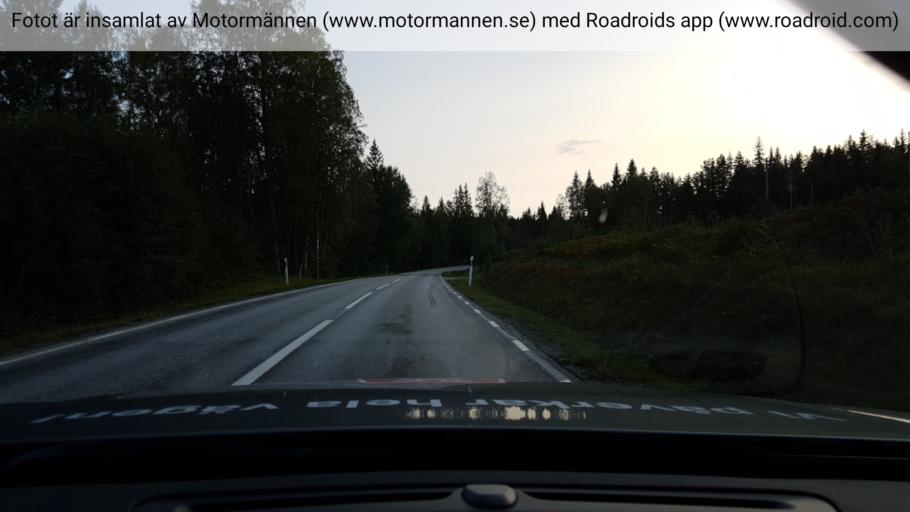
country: SE
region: OErebro
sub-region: Ljusnarsbergs Kommun
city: Kopparberg
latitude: 59.8187
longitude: 14.9625
